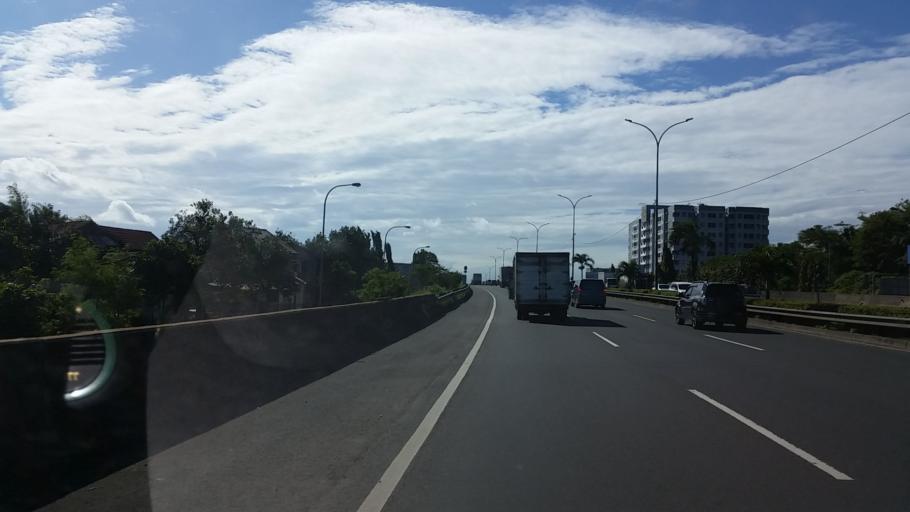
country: ID
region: Banten
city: South Tangerang
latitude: -6.2591
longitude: 106.7661
